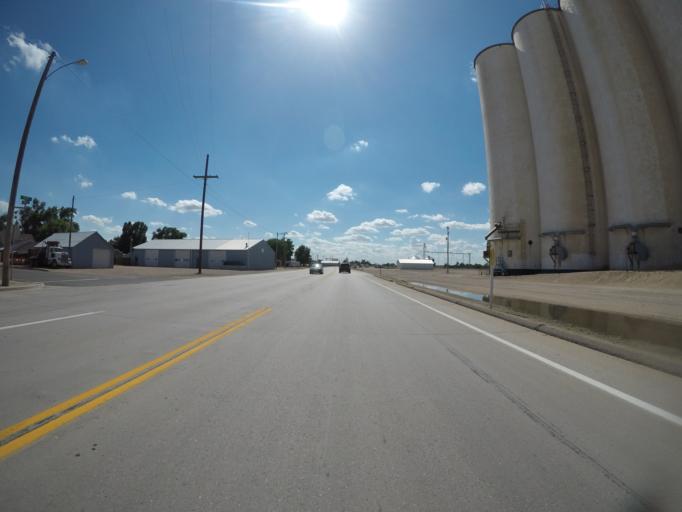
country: US
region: Colorado
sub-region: Phillips County
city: Holyoke
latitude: 40.5855
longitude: -102.3062
